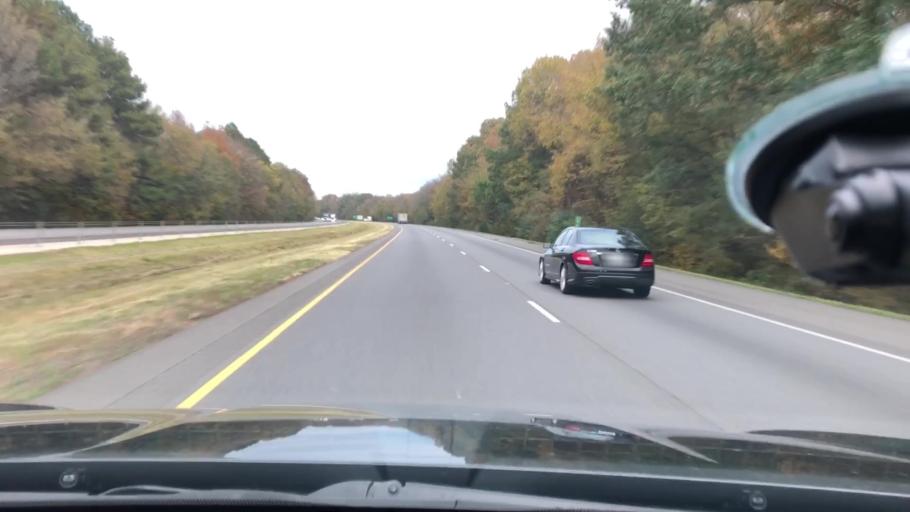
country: US
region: Arkansas
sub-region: Hot Spring County
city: Malvern
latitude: 34.3672
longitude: -92.8649
